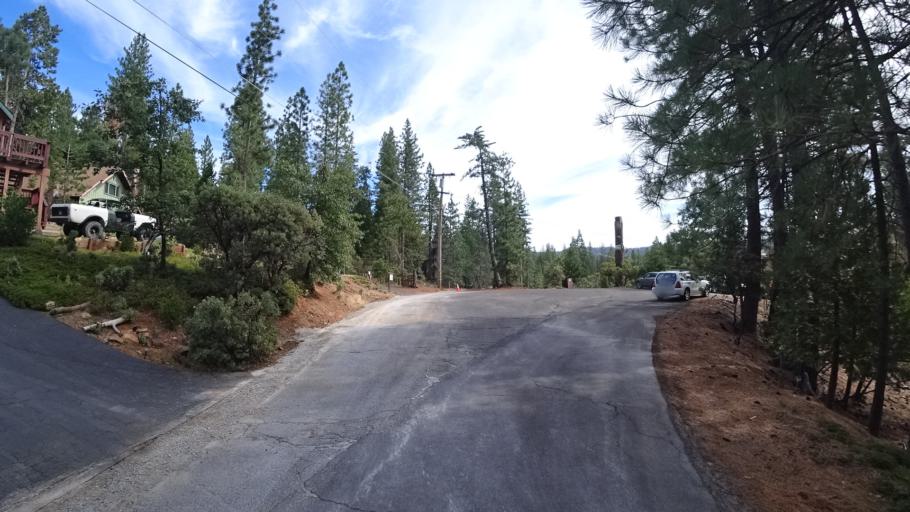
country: US
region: California
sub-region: Calaveras County
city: Arnold
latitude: 38.2461
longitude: -120.3429
